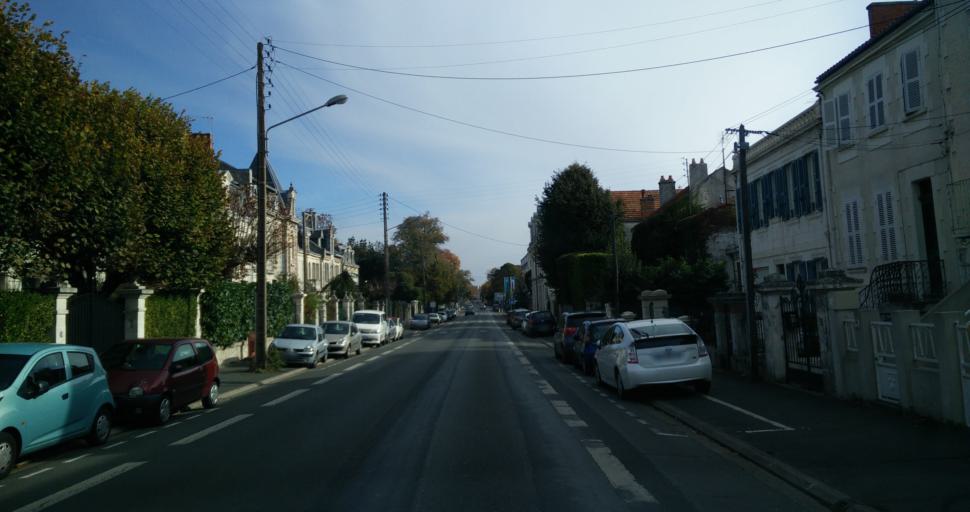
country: FR
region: Poitou-Charentes
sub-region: Departement de la Charente-Maritime
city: La Rochelle
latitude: 46.1629
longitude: -1.1629
